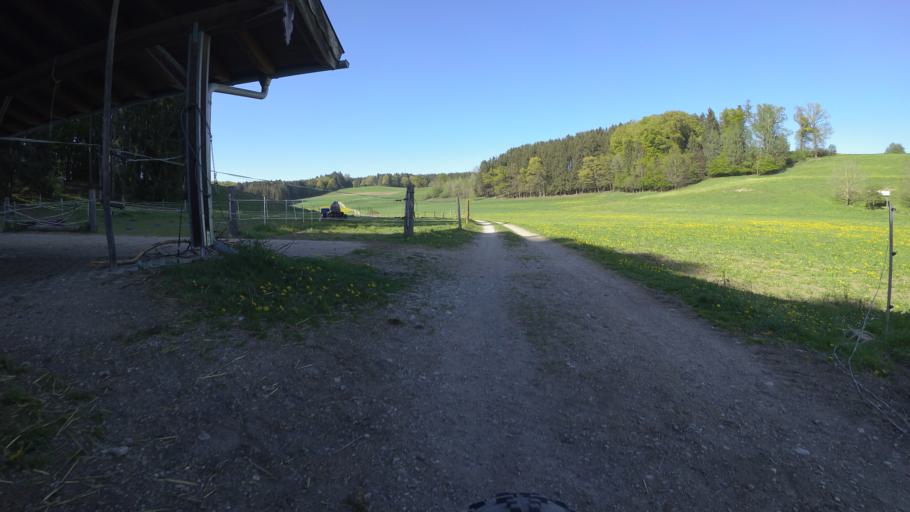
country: DE
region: Bavaria
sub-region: Upper Bavaria
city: Grabenstatt
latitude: 47.8637
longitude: 12.5701
